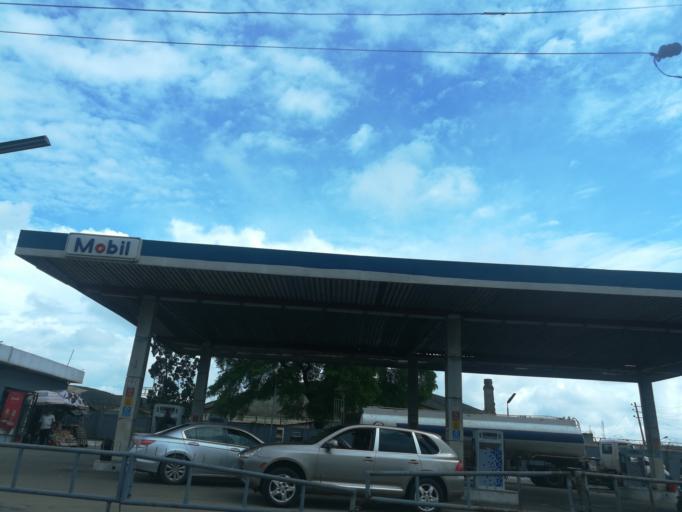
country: NG
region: Lagos
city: Agege
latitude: 6.6169
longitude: 3.3358
